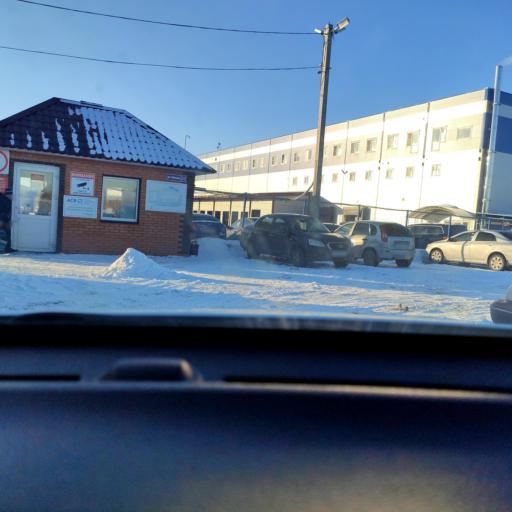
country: RU
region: Tatarstan
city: Stolbishchi
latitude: 55.6445
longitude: 49.2815
